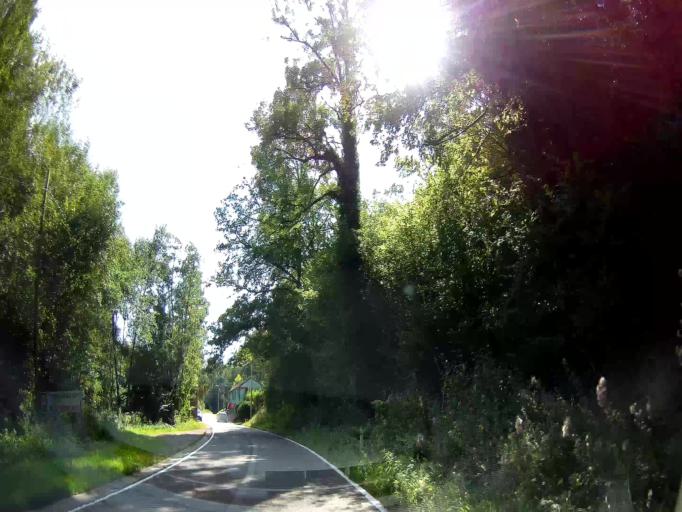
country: BE
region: Wallonia
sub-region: Province de Namur
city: Anhee
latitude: 50.3116
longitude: 4.8311
